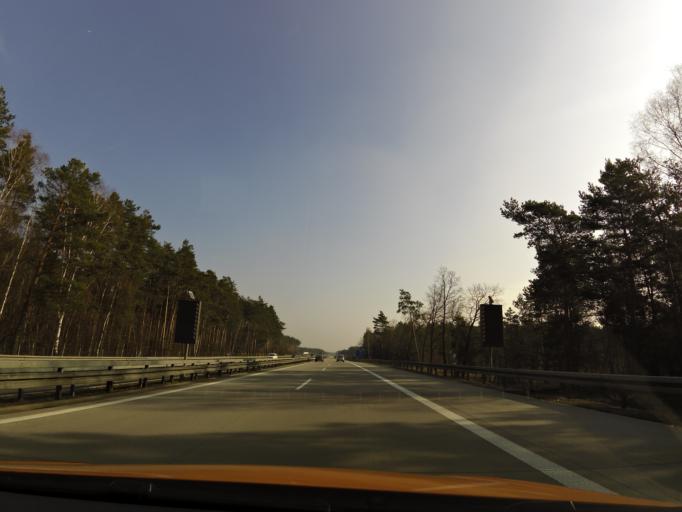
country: DE
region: Brandenburg
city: Berkenbruck
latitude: 52.3371
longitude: 14.2121
